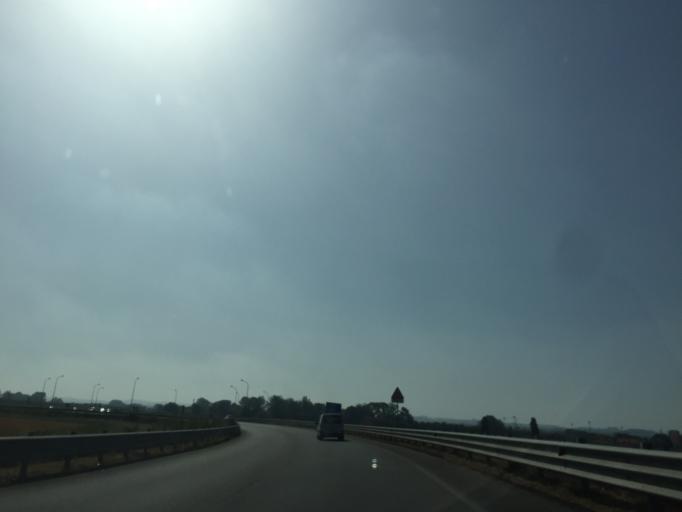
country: IT
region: Tuscany
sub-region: Province of Pisa
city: Pontedera
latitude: 43.6729
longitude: 10.6478
